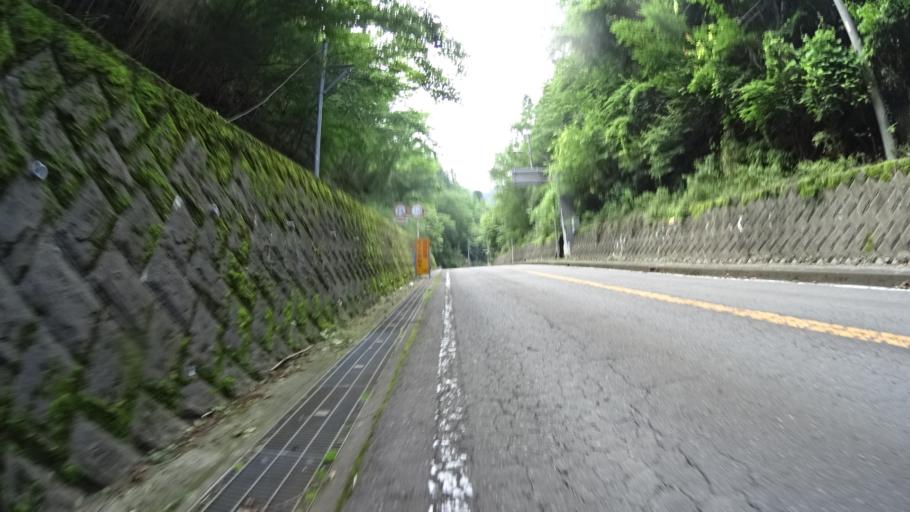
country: JP
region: Kanagawa
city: Hadano
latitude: 35.5017
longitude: 139.2310
